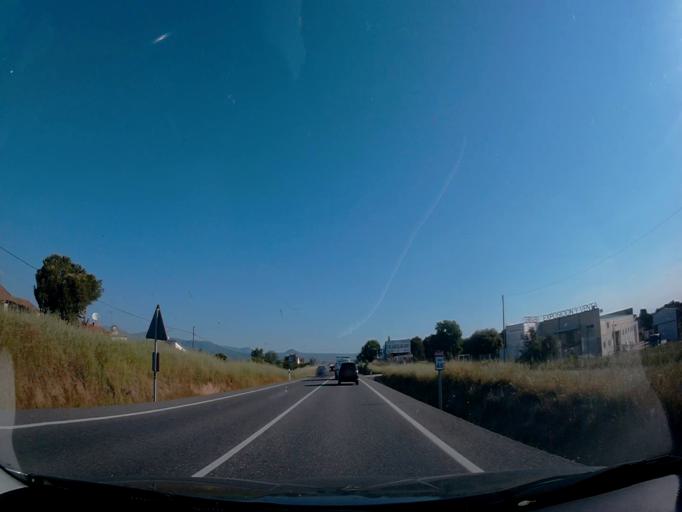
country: ES
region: Castille-La Mancha
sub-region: Province of Toledo
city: Escalona
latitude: 40.1295
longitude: -4.4052
